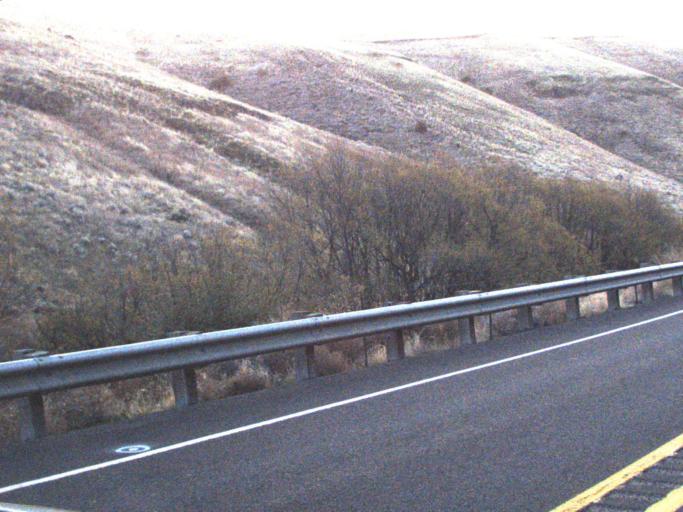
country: US
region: Washington
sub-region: Garfield County
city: Pomeroy
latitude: 46.6532
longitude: -117.8064
